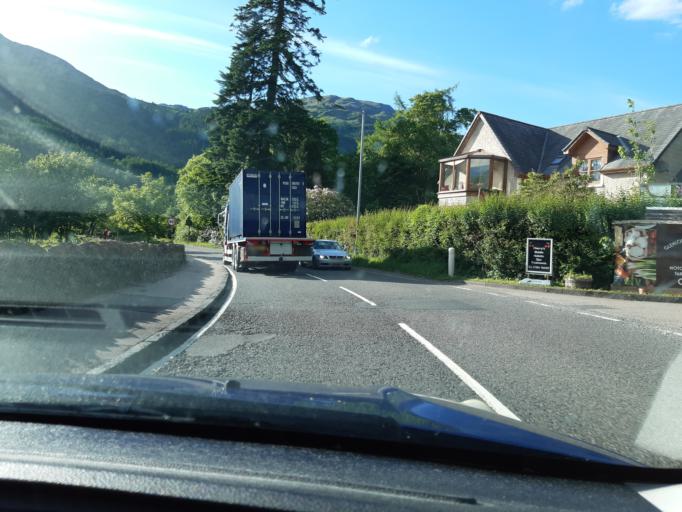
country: GB
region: Scotland
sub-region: Argyll and Bute
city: Garelochhead
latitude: 56.2064
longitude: -4.7444
